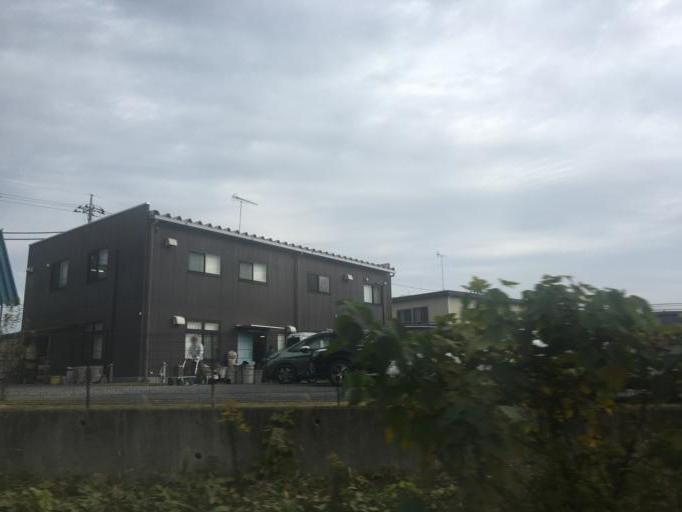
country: JP
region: Tokyo
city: Fussa
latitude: 35.7837
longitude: 139.3422
